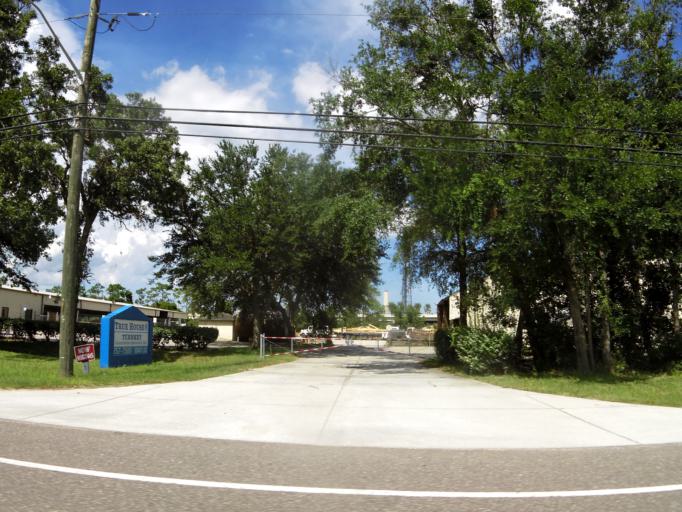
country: US
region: Florida
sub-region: Duval County
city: Jacksonville
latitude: 30.4191
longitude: -81.5686
